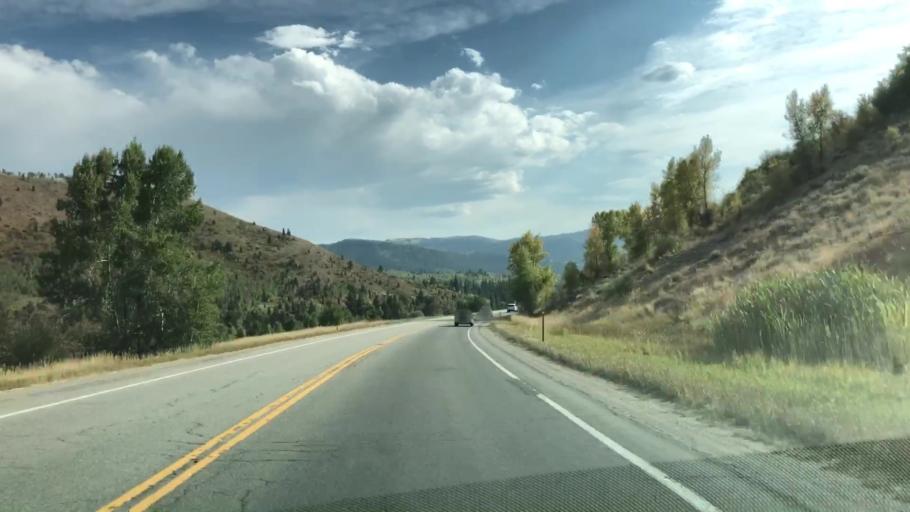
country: US
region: Wyoming
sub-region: Teton County
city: Hoback
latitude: 43.3522
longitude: -110.7201
